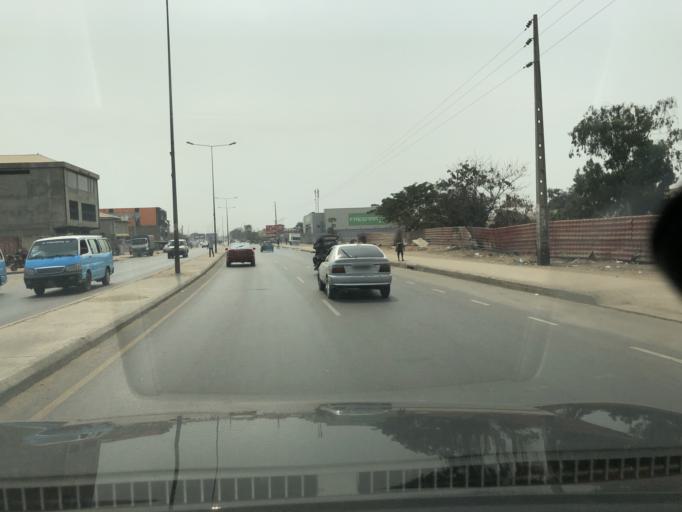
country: AO
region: Luanda
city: Luanda
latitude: -8.8005
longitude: 13.3126
